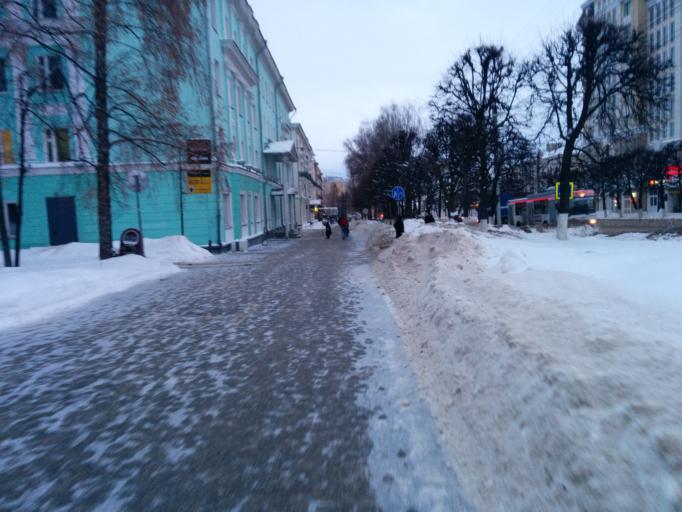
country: RU
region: Chuvashia
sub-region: Cheboksarskiy Rayon
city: Cheboksary
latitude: 56.1294
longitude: 47.2478
